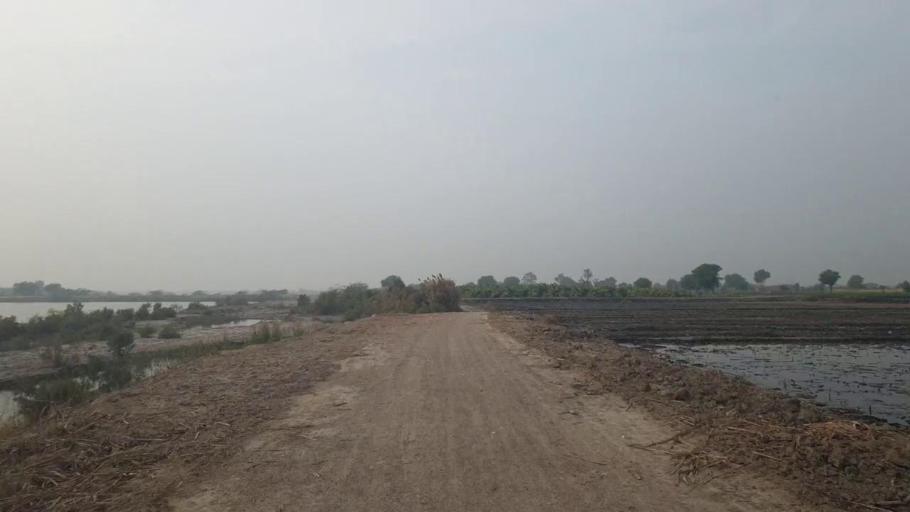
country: PK
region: Sindh
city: Berani
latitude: 25.8241
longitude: 68.7326
